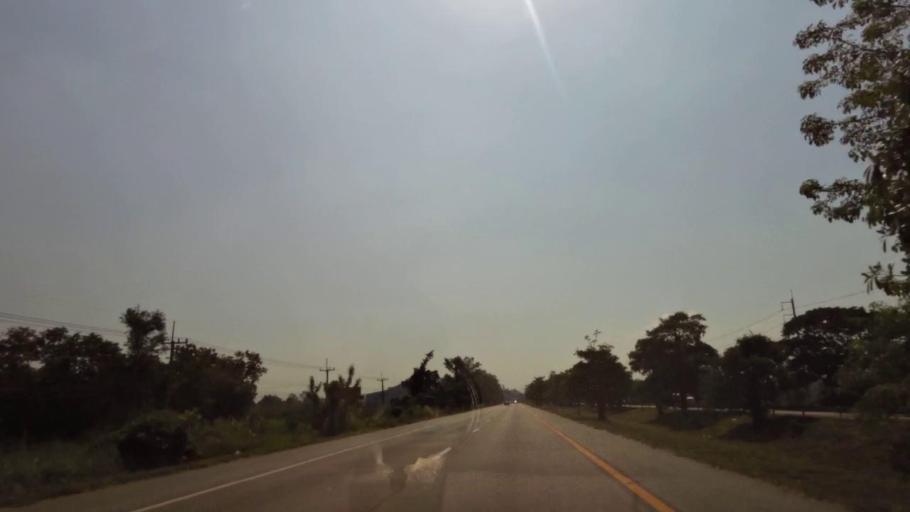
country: TH
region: Phichit
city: Wachira Barami
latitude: 16.6260
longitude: 100.1500
